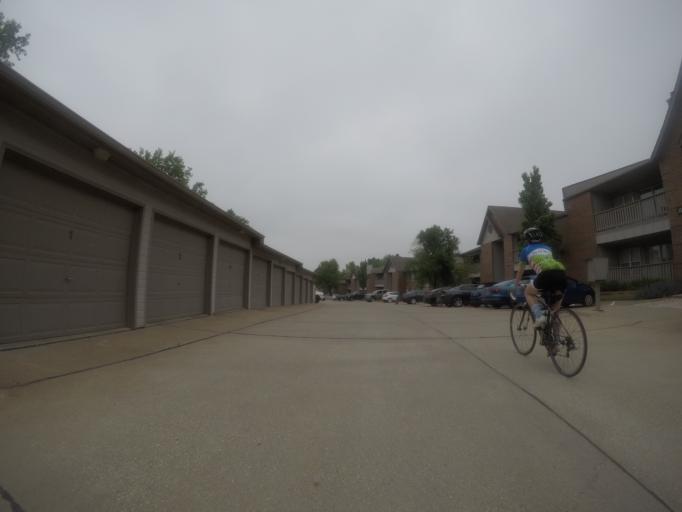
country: US
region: Kansas
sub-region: Riley County
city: Manhattan
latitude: 39.1950
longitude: -96.6039
